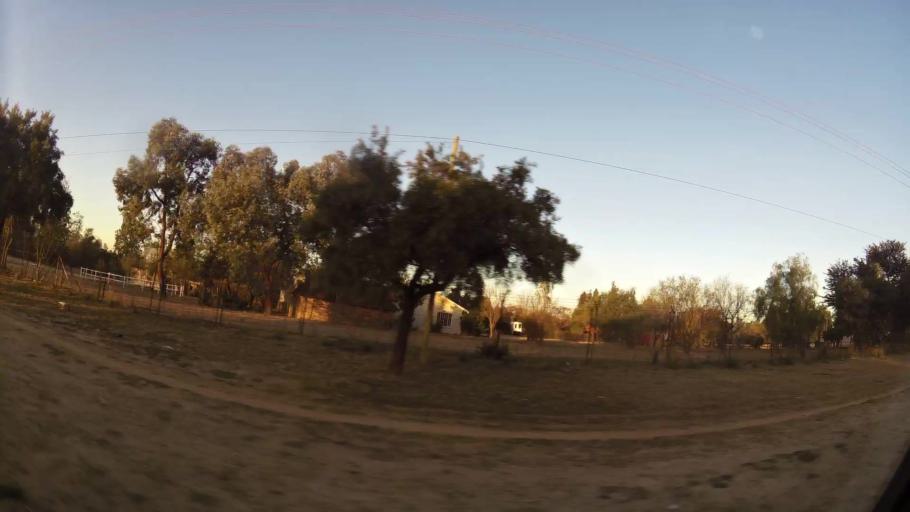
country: ZA
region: Gauteng
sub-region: City of Johannesburg Metropolitan Municipality
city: Diepsloot
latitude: -25.9698
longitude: 28.0467
